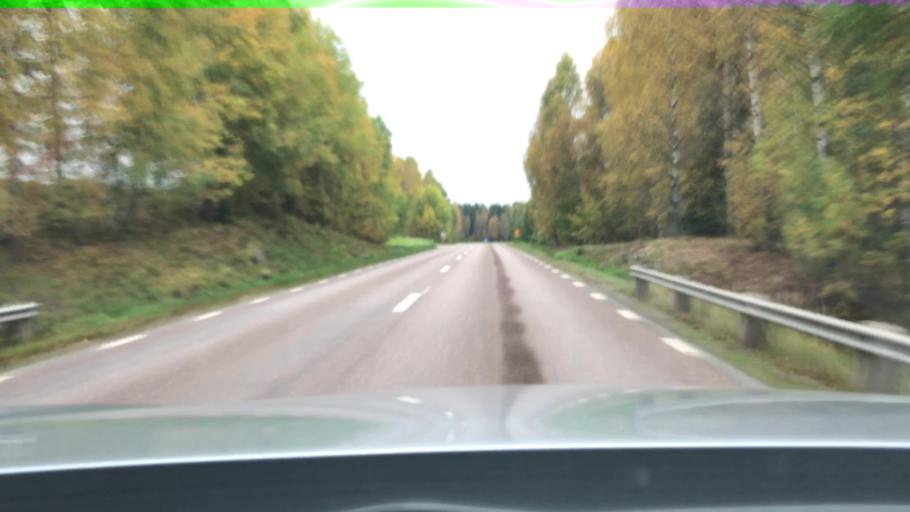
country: SE
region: Vaermland
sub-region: Eda Kommun
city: Amotfors
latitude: 59.7367
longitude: 12.2077
